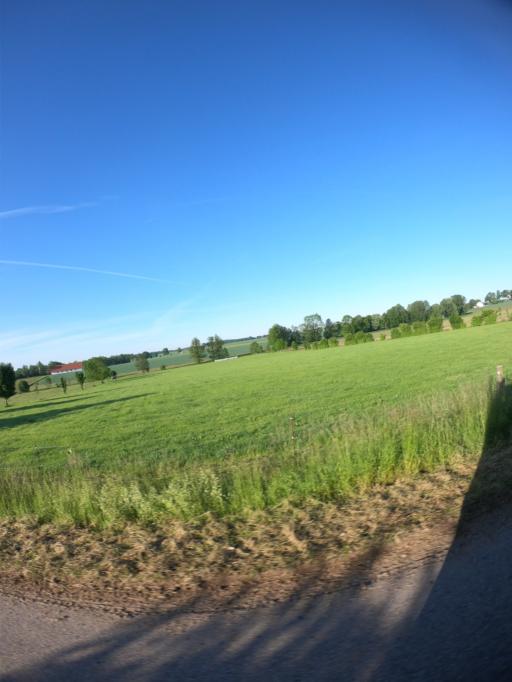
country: DE
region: Bavaria
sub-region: Upper Bavaria
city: Bockhorn
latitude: 48.3082
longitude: 11.9537
